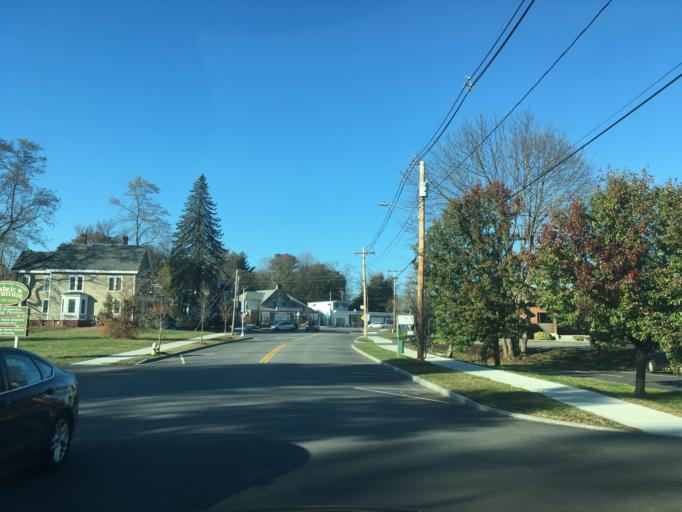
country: US
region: New Hampshire
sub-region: Rockingham County
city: Exeter
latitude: 42.9804
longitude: -70.9574
